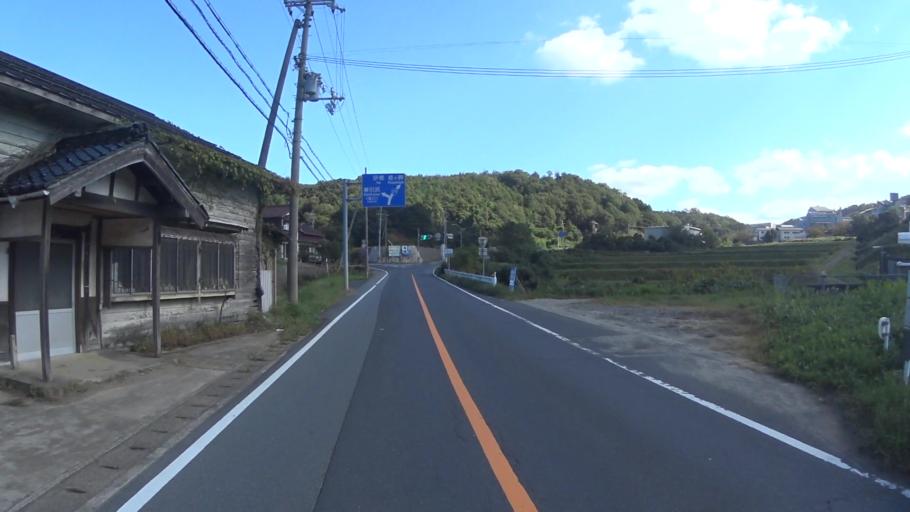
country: JP
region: Kyoto
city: Miyazu
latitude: 35.7004
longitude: 135.0615
